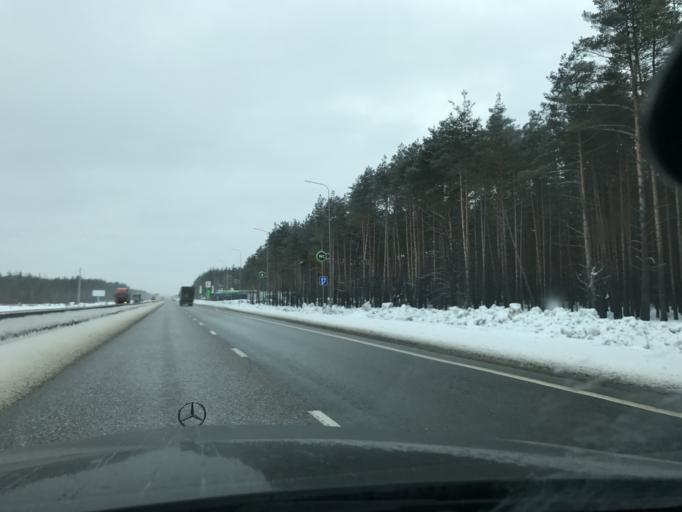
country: RU
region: Nizjnij Novgorod
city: Mulino
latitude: 56.2628
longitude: 42.9228
